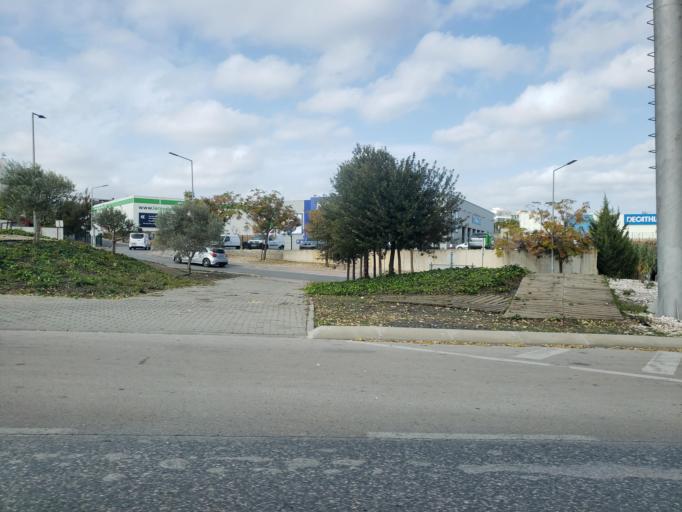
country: PT
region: Faro
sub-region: Portimao
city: Portimao
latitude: 37.1474
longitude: -8.5486
